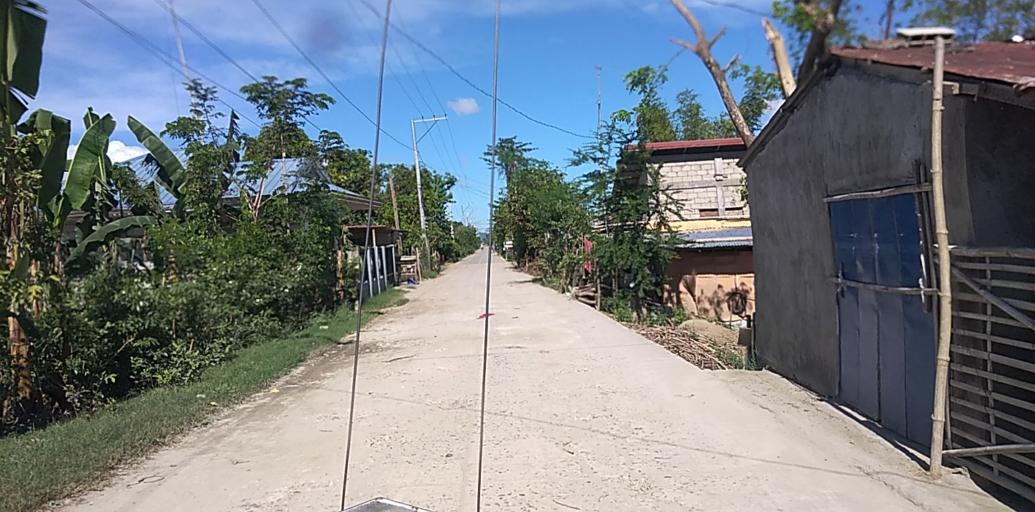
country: PH
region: Central Luzon
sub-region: Province of Pampanga
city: Candating
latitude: 15.1252
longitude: 120.8112
